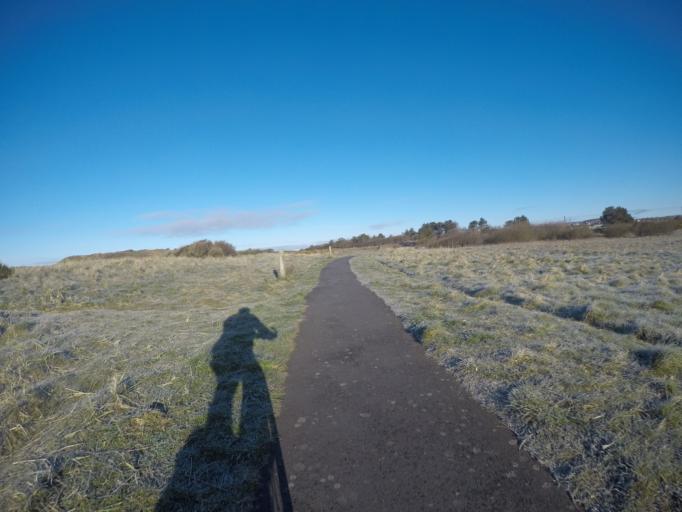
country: GB
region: Scotland
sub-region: North Ayrshire
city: Stevenston
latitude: 55.6314
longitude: -4.7584
